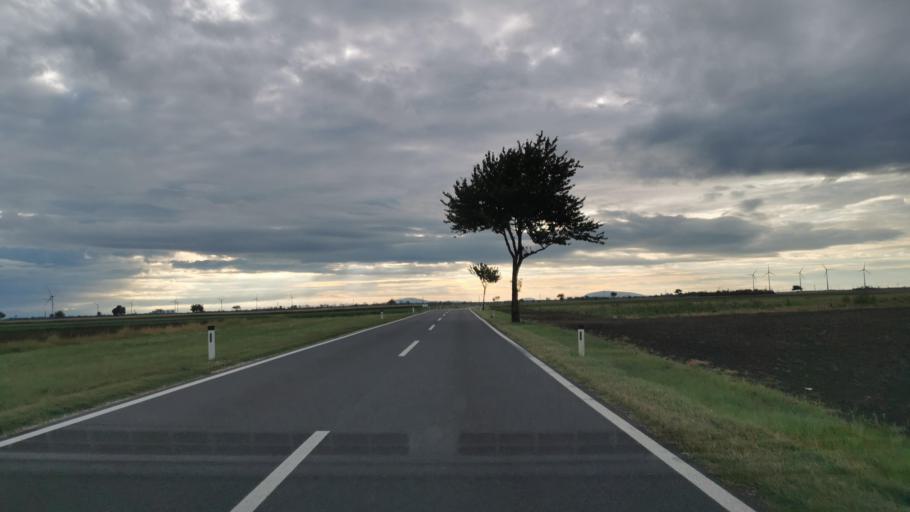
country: AT
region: Lower Austria
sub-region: Politischer Bezirk Ganserndorf
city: Glinzendorf
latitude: 48.2286
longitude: 16.6275
